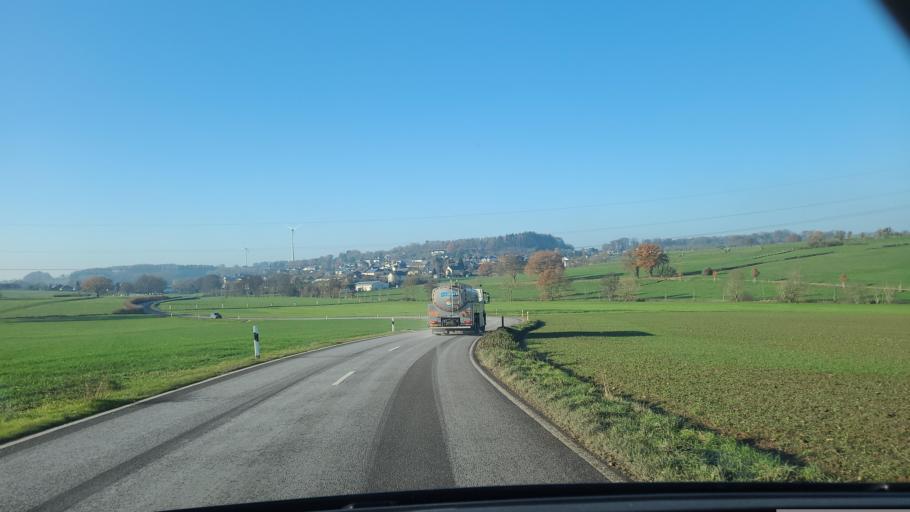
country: LU
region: Luxembourg
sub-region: Canton de Capellen
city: Garnich
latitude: 49.6139
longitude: 5.9672
